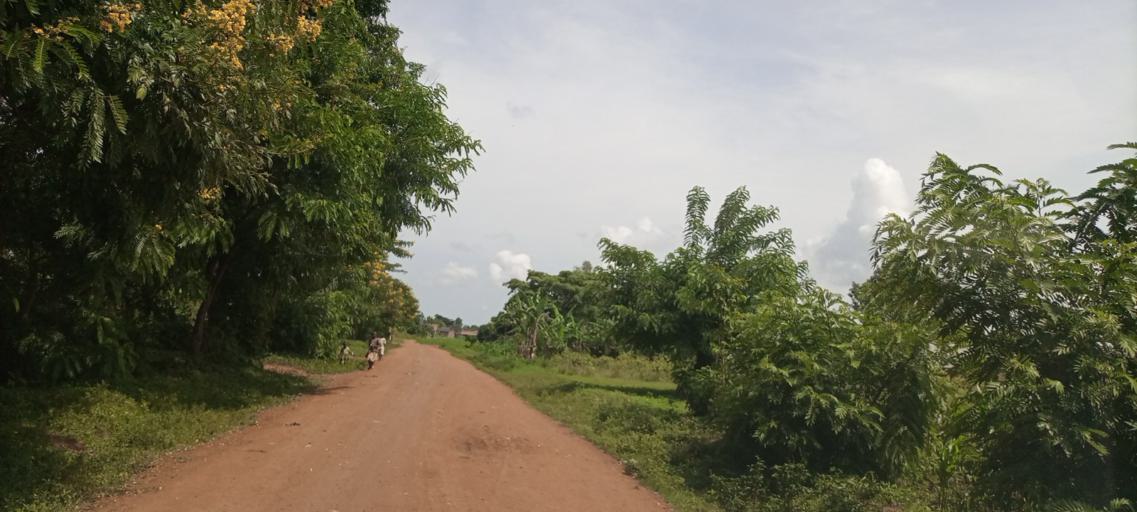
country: UG
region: Eastern Region
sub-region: Budaka District
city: Budaka
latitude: 1.1709
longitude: 33.9366
